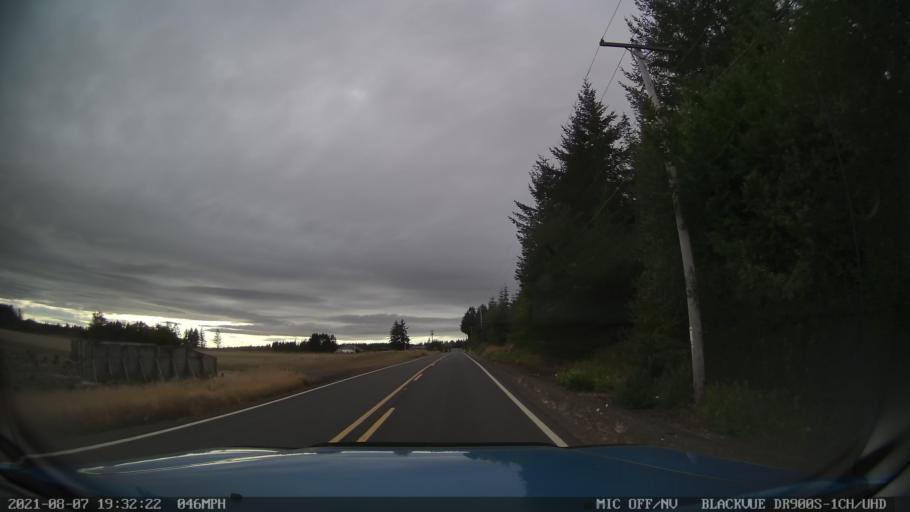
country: US
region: Oregon
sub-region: Linn County
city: Lyons
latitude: 44.8994
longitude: -122.6428
